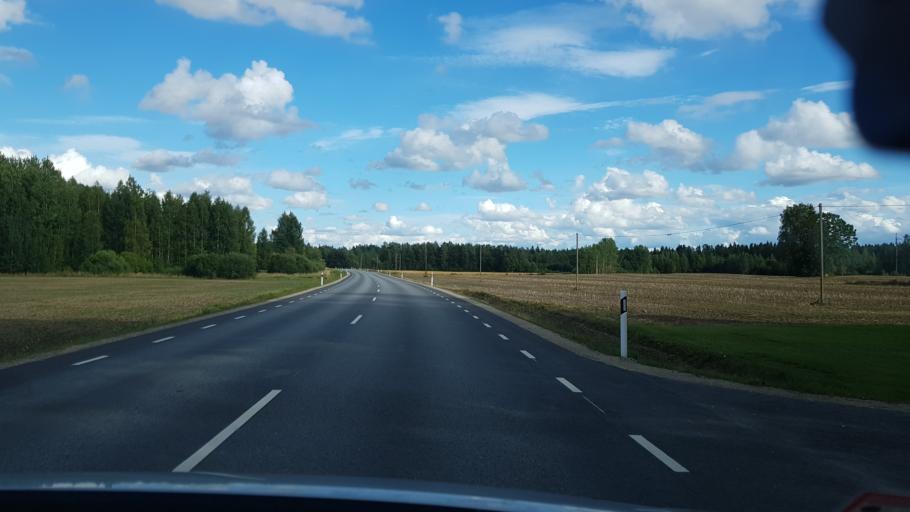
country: EE
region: Polvamaa
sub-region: Polva linn
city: Polva
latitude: 58.0767
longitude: 27.2493
